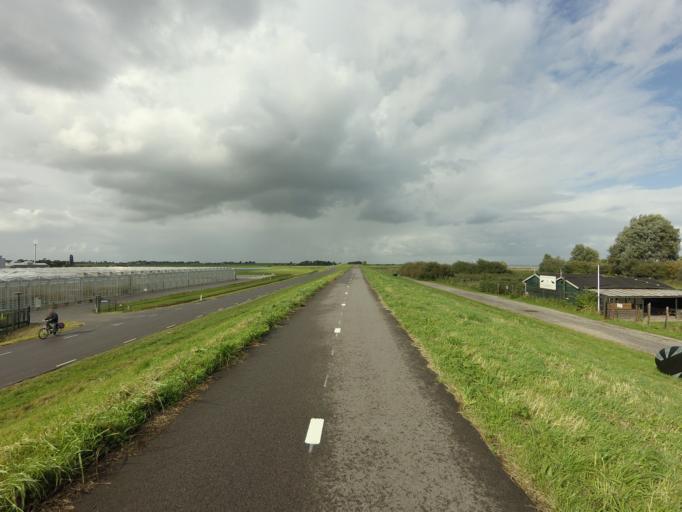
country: NL
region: North Holland
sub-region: Gemeente Enkhuizen
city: Enkhuizen
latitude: 52.7257
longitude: 5.2832
